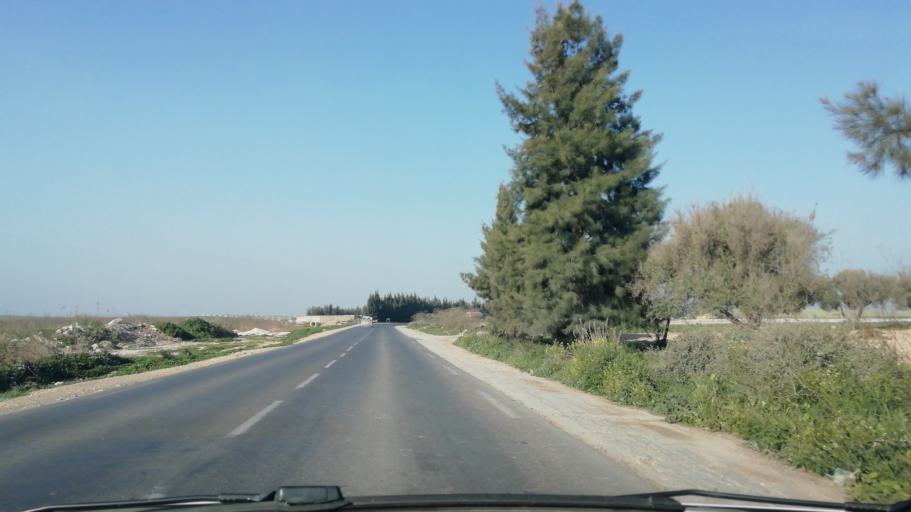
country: DZ
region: Mostaganem
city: Mostaganem
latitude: 35.7446
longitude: 0.1473
